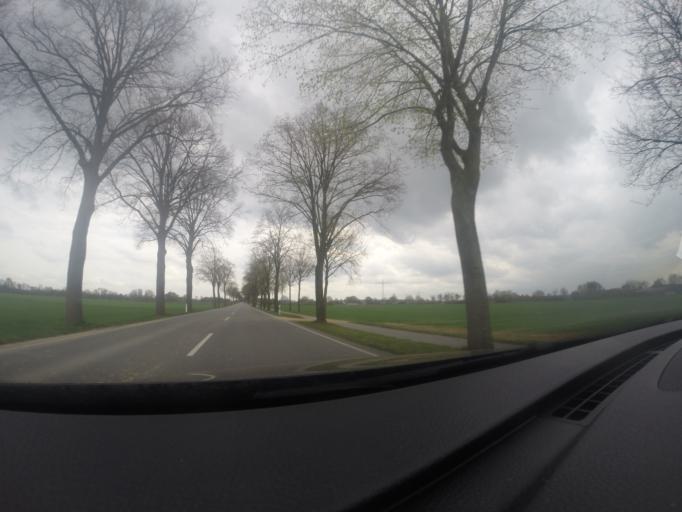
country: DE
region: North Rhine-Westphalia
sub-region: Regierungsbezirk Dusseldorf
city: Xanten
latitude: 51.6833
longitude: 6.4089
